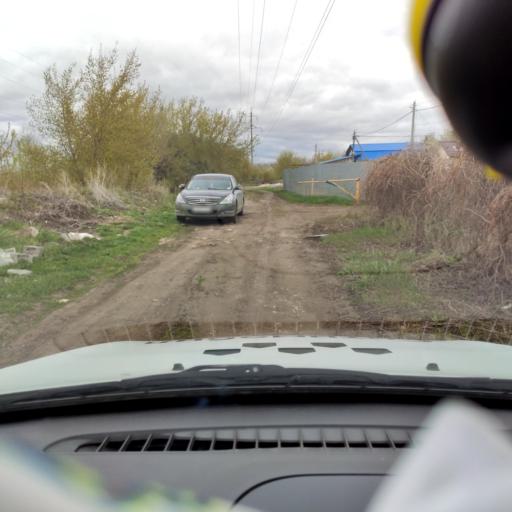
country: RU
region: Samara
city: Tol'yatti
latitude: 53.5864
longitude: 49.3231
